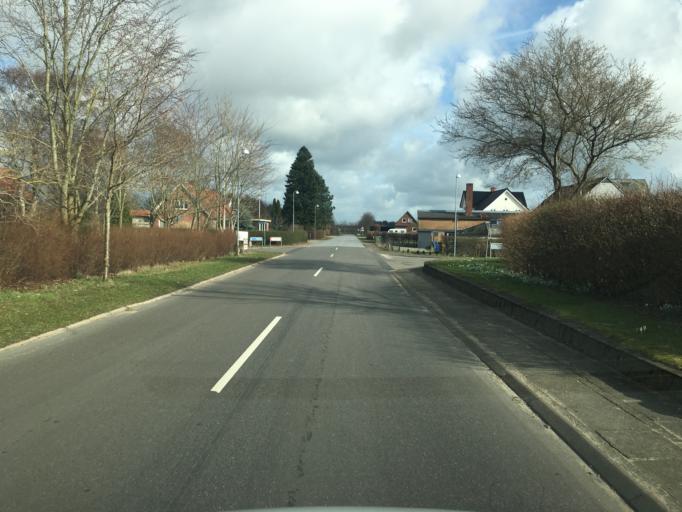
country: DK
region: South Denmark
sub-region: Aabenraa Kommune
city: Krusa
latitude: 54.8971
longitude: 9.4433
